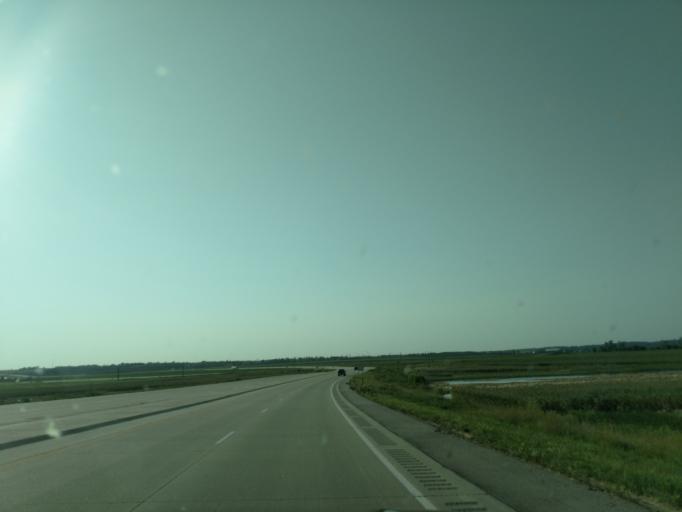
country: US
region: Nebraska
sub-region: Sarpy County
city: Offutt Air Force Base
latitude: 41.0721
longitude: -95.8860
